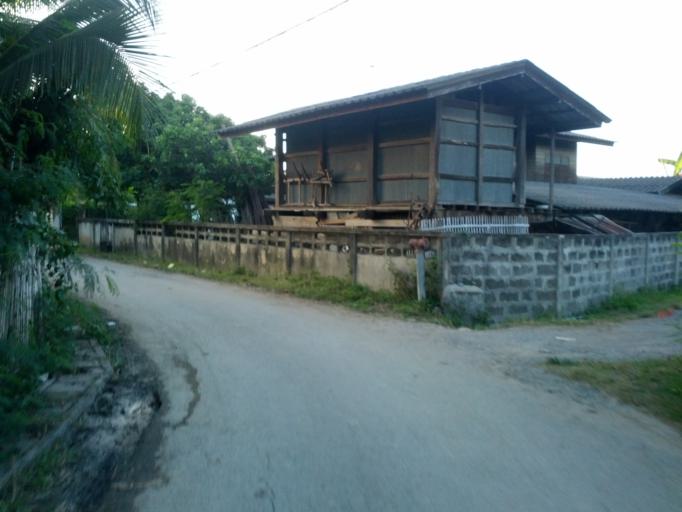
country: TH
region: Chiang Mai
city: San Kamphaeng
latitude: 18.7711
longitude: 99.1175
